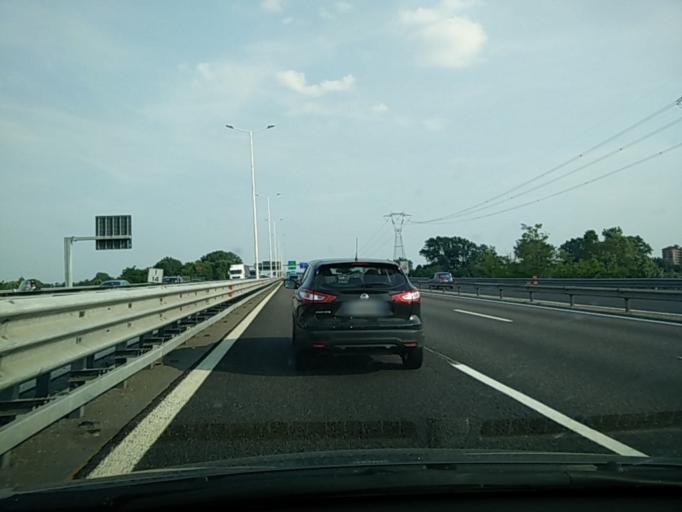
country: IT
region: Lombardy
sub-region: Citta metropolitana di Milano
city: Trezzano sul Naviglio
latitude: 45.4266
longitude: 9.0775
